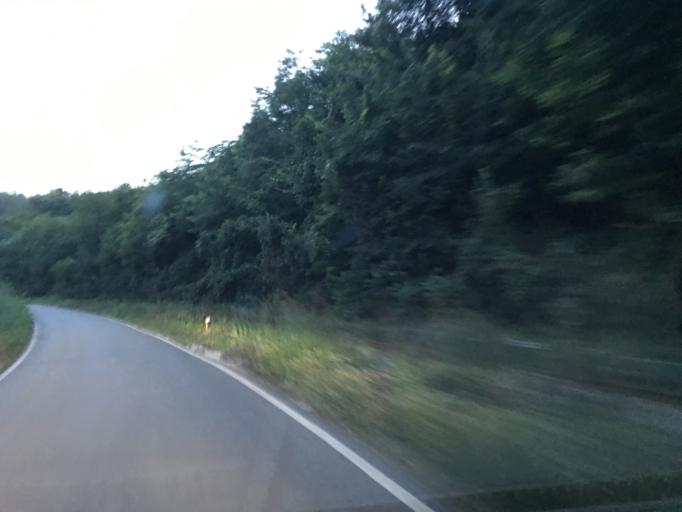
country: BG
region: Vidin
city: Bregovo
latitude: 44.1403
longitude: 22.6033
